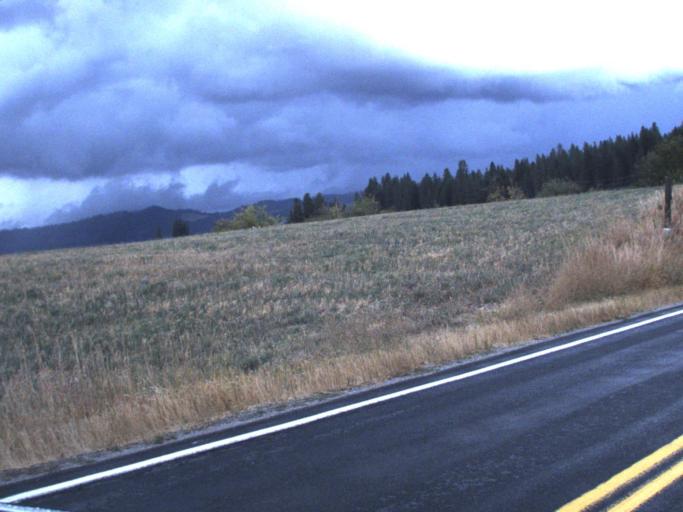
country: US
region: Washington
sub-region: Stevens County
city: Chewelah
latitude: 48.1231
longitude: -117.7489
